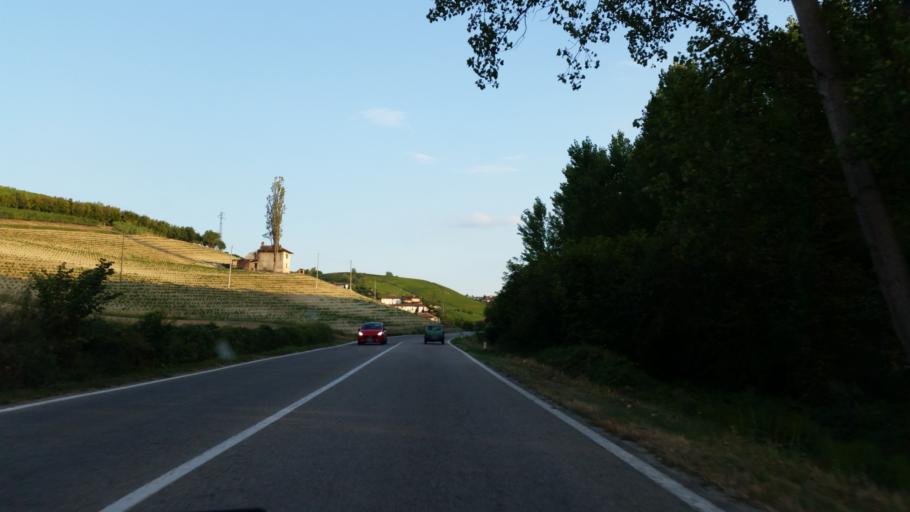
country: IT
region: Piedmont
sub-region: Provincia di Cuneo
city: Barbaresco
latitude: 44.7379
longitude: 8.0937
